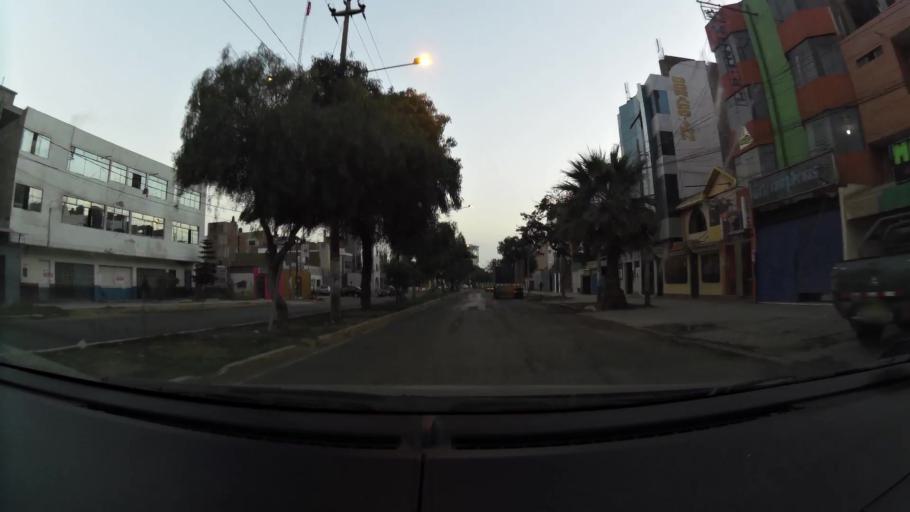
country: PE
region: La Libertad
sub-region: Provincia de Trujillo
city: Trujillo
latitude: -8.0981
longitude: -79.0204
